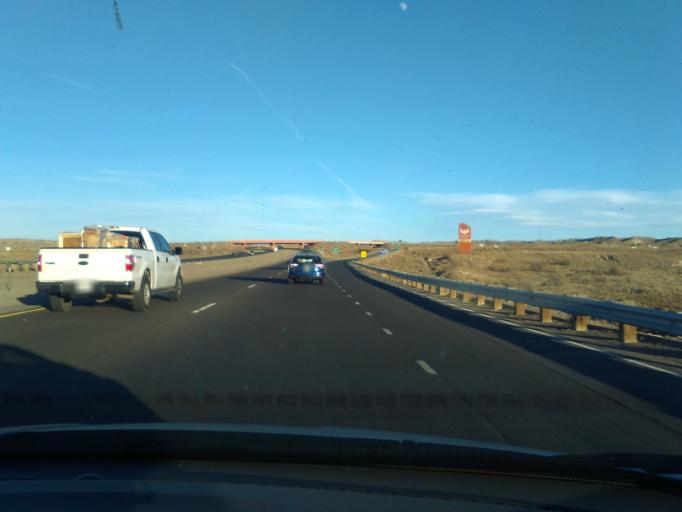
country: US
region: New Mexico
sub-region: Bernalillo County
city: South Valley
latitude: 34.9512
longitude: -106.6718
